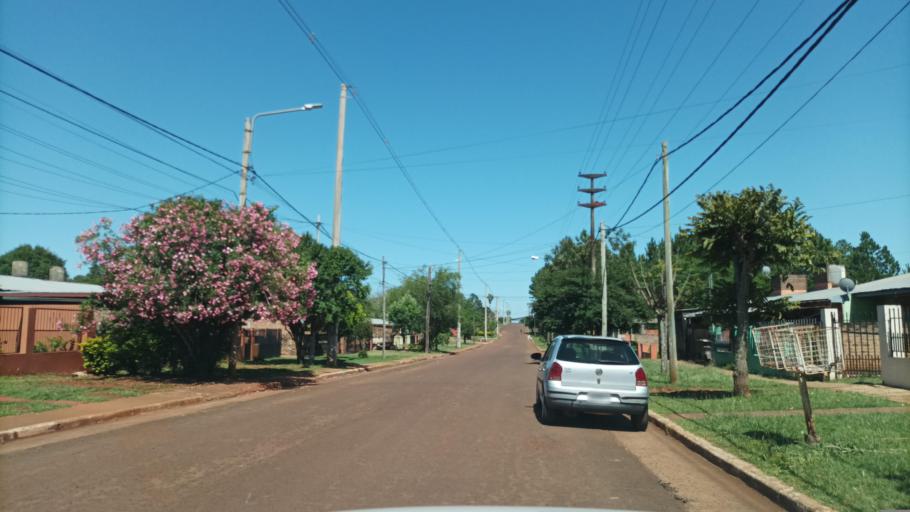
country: AR
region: Misiones
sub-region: Departamento de Apostoles
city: San Jose
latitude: -27.7661
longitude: -55.7741
